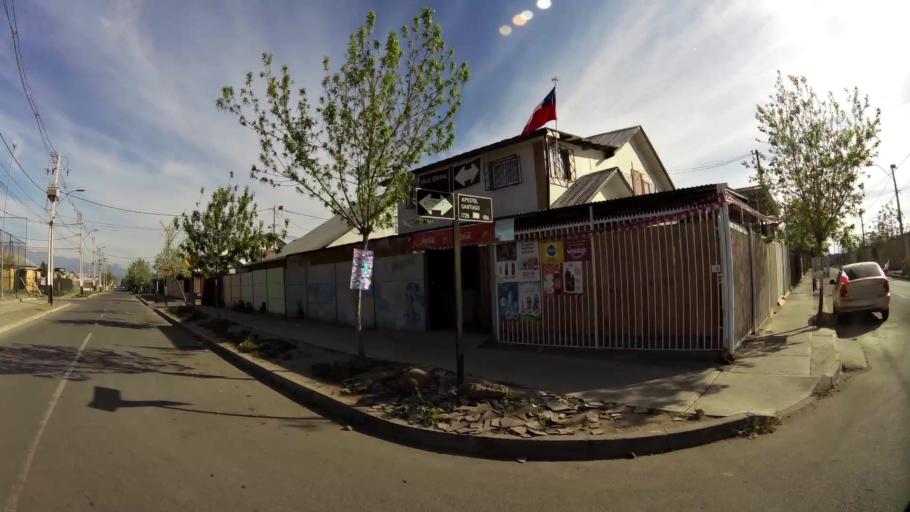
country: CL
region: Santiago Metropolitan
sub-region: Provincia de Cordillera
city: Puente Alto
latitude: -33.6160
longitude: -70.5979
